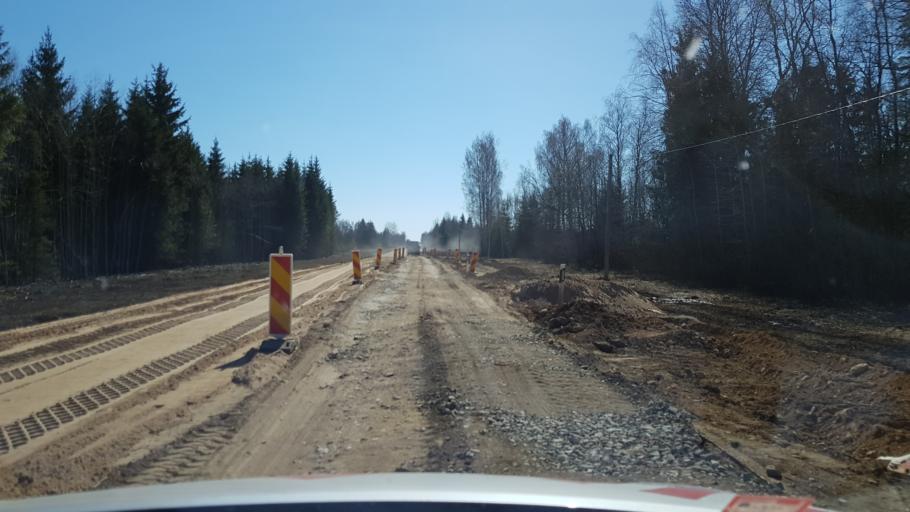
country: EE
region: Jogevamaa
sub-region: Mustvee linn
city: Mustvee
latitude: 59.0353
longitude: 26.6826
